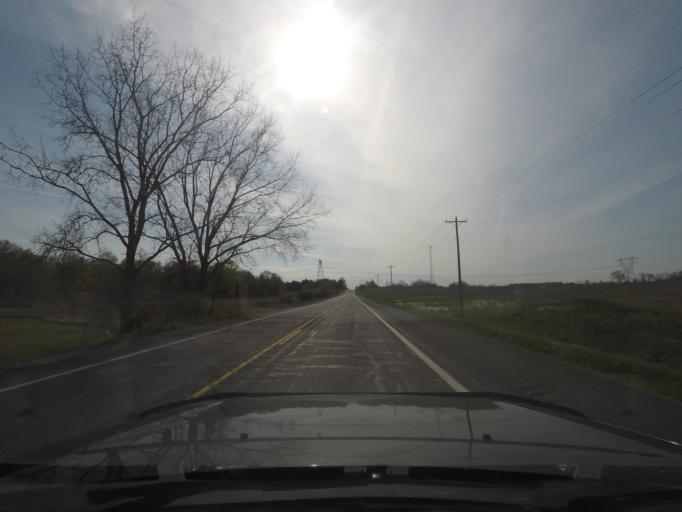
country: US
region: Indiana
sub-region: LaPorte County
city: Hudson Lake
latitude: 41.7982
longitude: -86.5201
